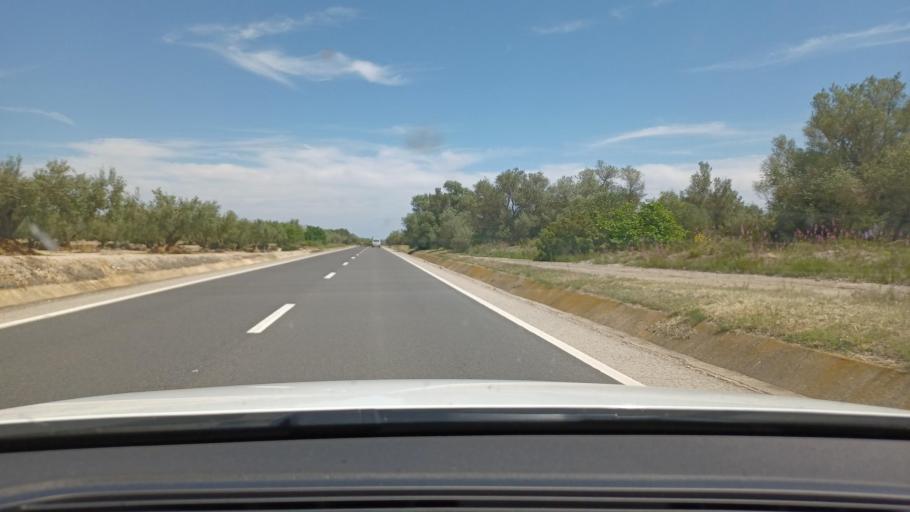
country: ES
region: Catalonia
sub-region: Provincia de Tarragona
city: Ulldecona
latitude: 40.6570
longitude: 0.4079
